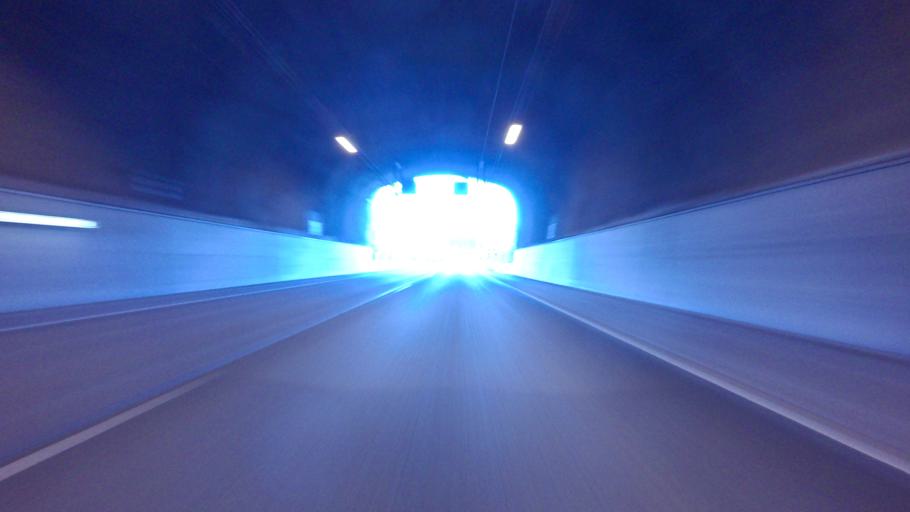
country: FI
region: Uusimaa
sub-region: Helsinki
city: Saukkola
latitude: 60.3121
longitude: 23.9923
